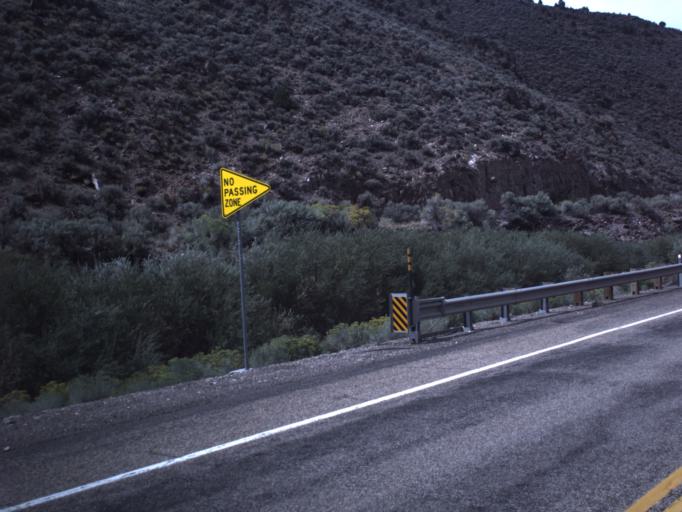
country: US
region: Utah
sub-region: Piute County
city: Junction
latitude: 38.1351
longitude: -112.3155
